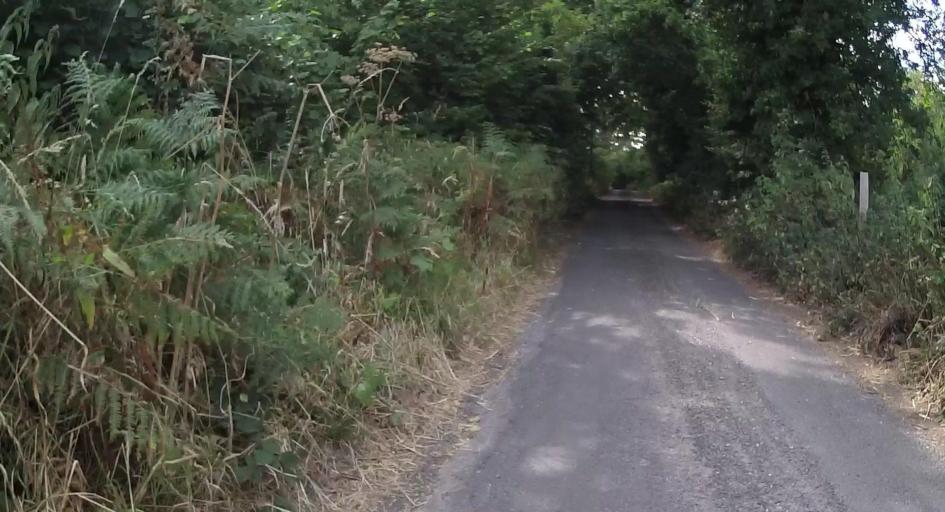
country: GB
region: England
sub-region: Dorset
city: Swanage
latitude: 50.6319
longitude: -2.0186
